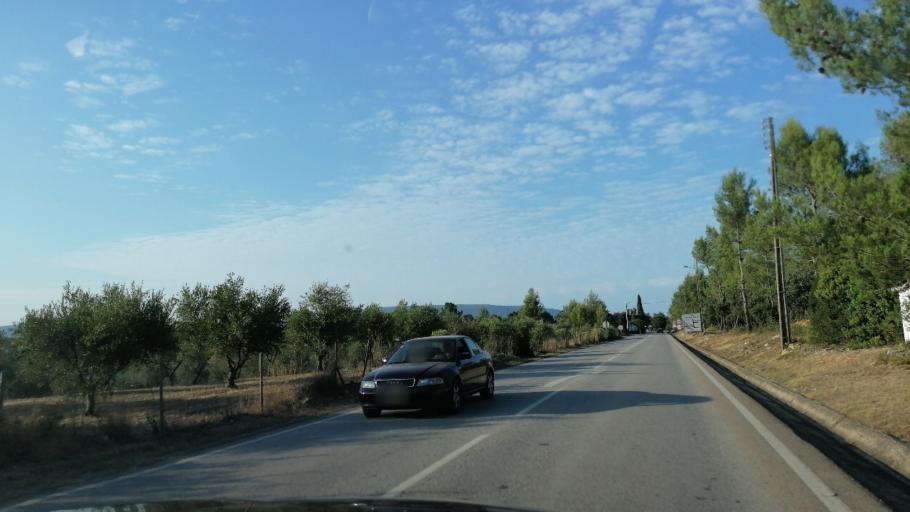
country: PT
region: Santarem
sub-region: Alcanena
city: Alcanena
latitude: 39.4274
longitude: -8.6338
